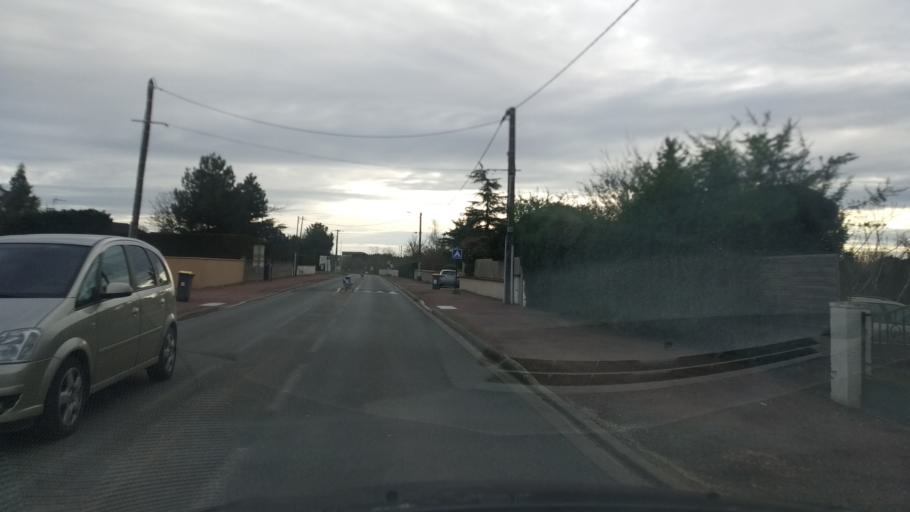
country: FR
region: Poitou-Charentes
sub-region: Departement de la Vienne
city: Dissay
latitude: 46.6890
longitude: 0.4164
